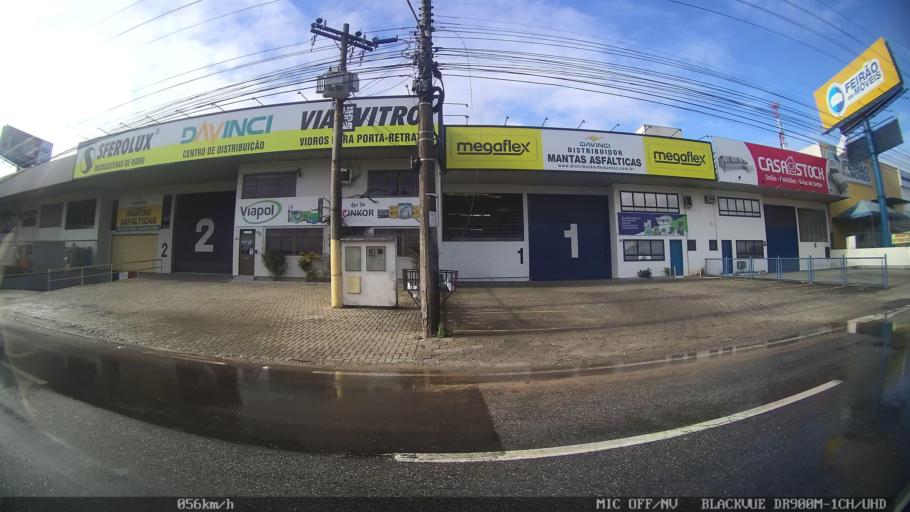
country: BR
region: Santa Catarina
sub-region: Sao Jose
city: Campinas
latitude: -27.6066
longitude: -48.6352
